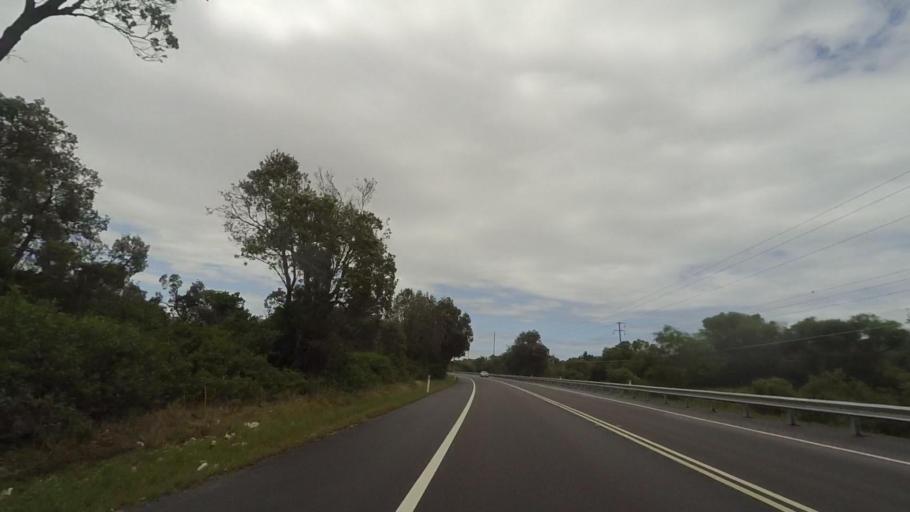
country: AU
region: New South Wales
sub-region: Wyong Shire
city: The Entrance
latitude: -33.3179
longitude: 151.5175
